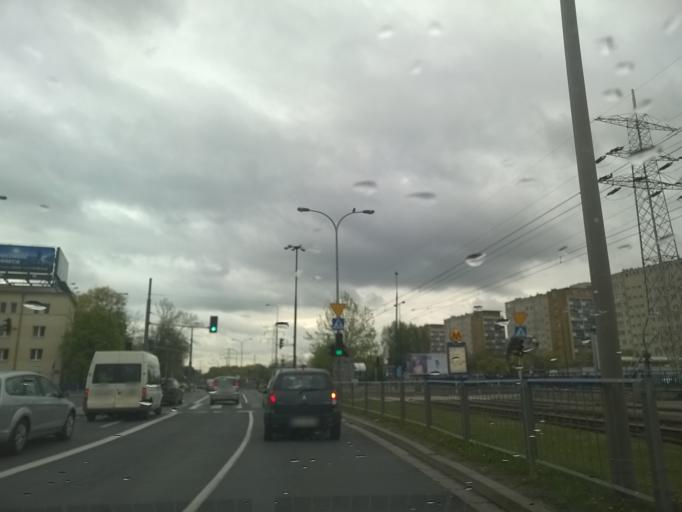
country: PL
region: Masovian Voivodeship
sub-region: Warszawa
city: Mokotow
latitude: 52.1890
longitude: 21.0162
